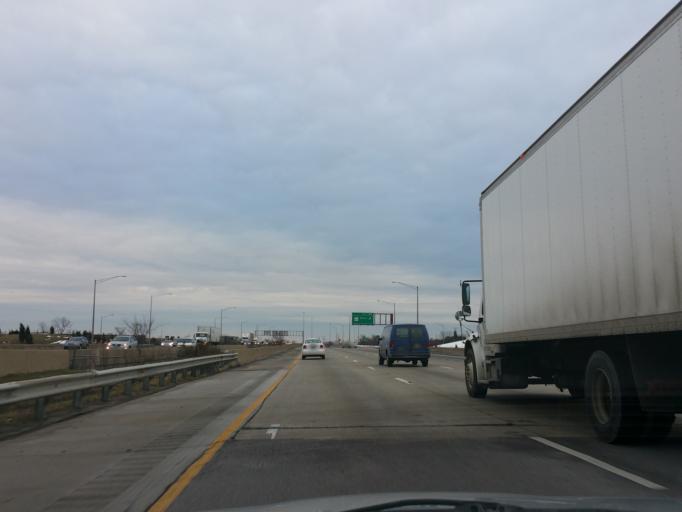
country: US
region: Illinois
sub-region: DuPage County
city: Addison
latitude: 41.9277
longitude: -87.9681
